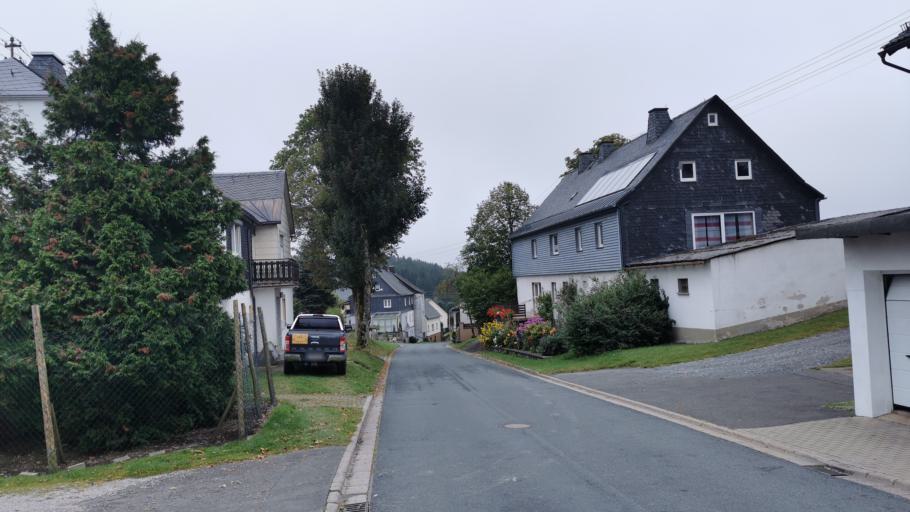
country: DE
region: Bavaria
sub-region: Upper Franconia
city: Reichenbach
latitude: 50.4316
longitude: 11.3995
